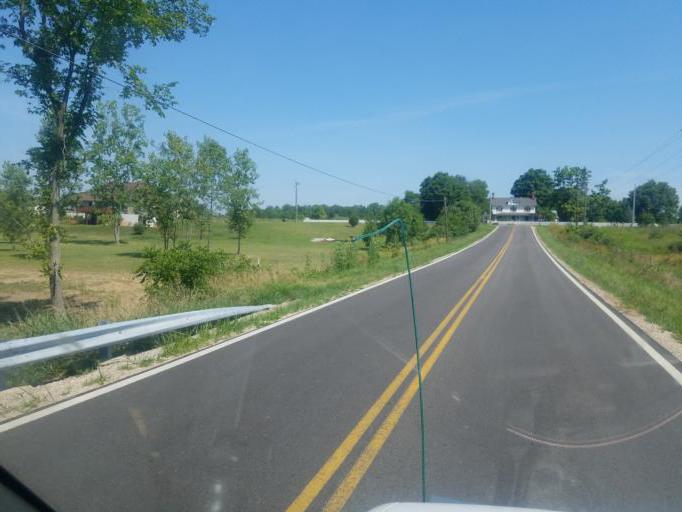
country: US
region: Ohio
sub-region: Union County
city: Marysville
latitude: 40.2233
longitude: -83.4555
